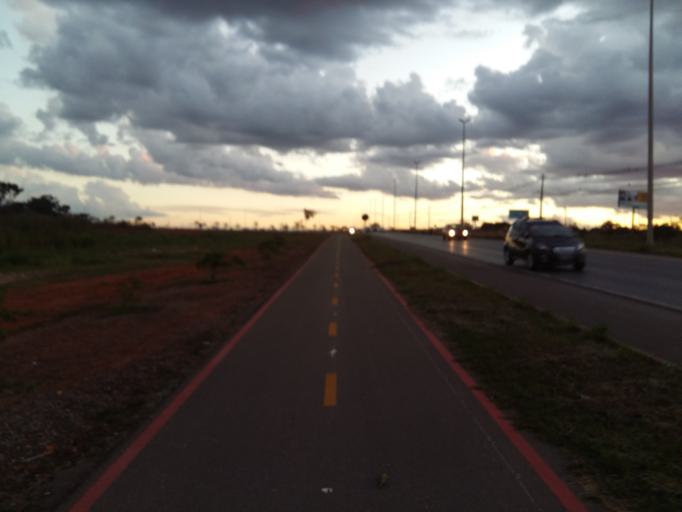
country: BR
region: Federal District
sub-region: Brasilia
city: Brasilia
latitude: -15.6852
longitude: -47.8549
